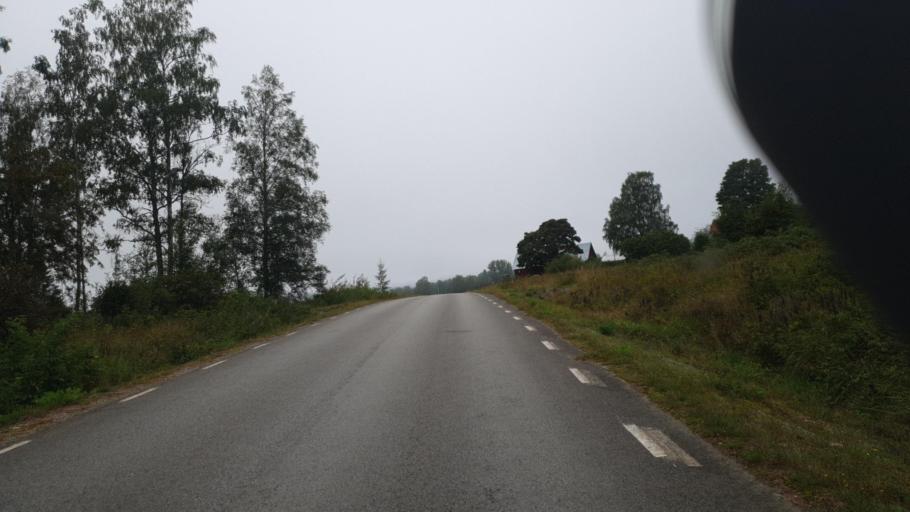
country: SE
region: Vaermland
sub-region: Eda Kommun
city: Amotfors
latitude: 59.7181
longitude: 12.4560
